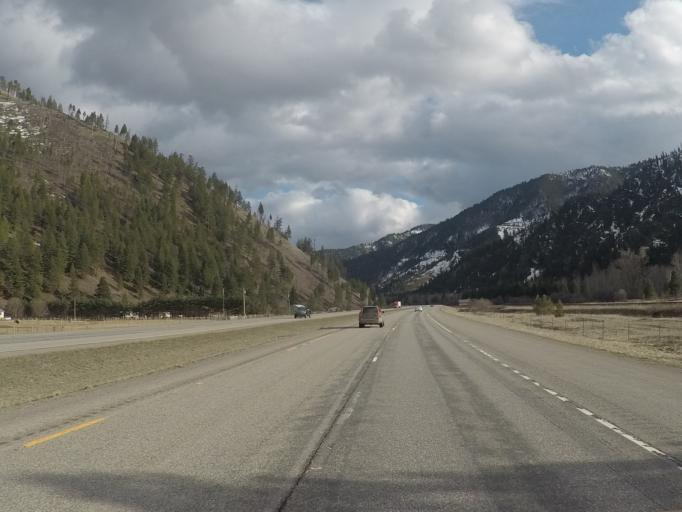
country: US
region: Montana
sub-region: Missoula County
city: Clinton
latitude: 46.7370
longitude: -113.6991
